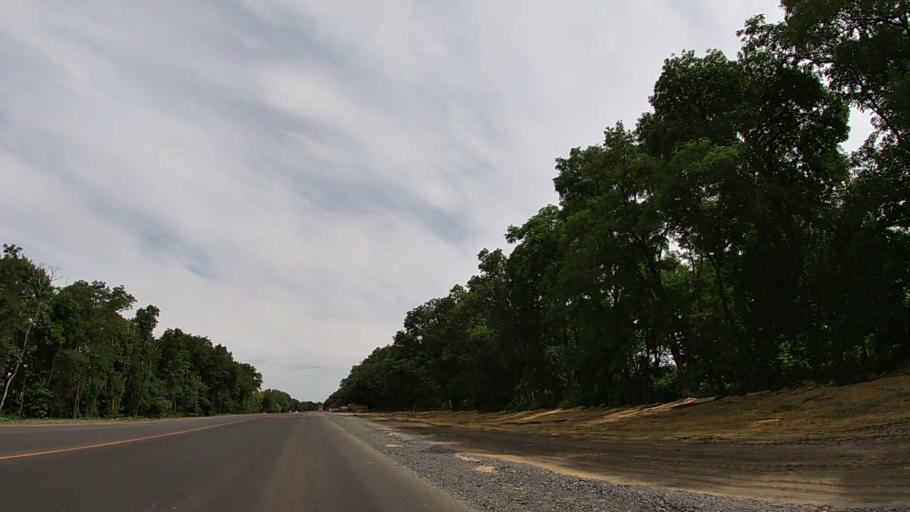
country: RU
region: Belgorod
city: Mayskiy
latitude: 50.4761
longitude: 36.4056
